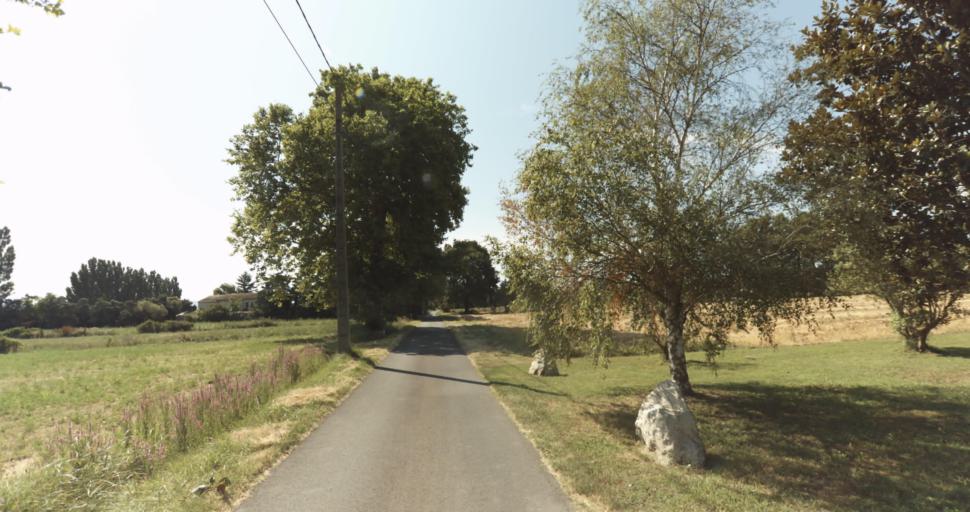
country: FR
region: Provence-Alpes-Cote d'Azur
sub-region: Departement du Vaucluse
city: Monteux
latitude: 44.0163
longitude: 5.0005
